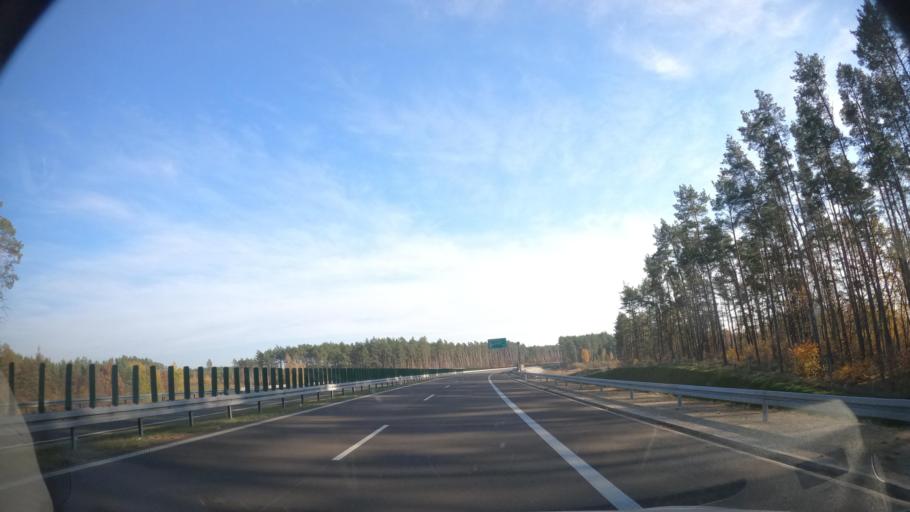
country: PL
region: West Pomeranian Voivodeship
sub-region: Powiat walecki
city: Walcz
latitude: 53.2929
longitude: 16.4976
